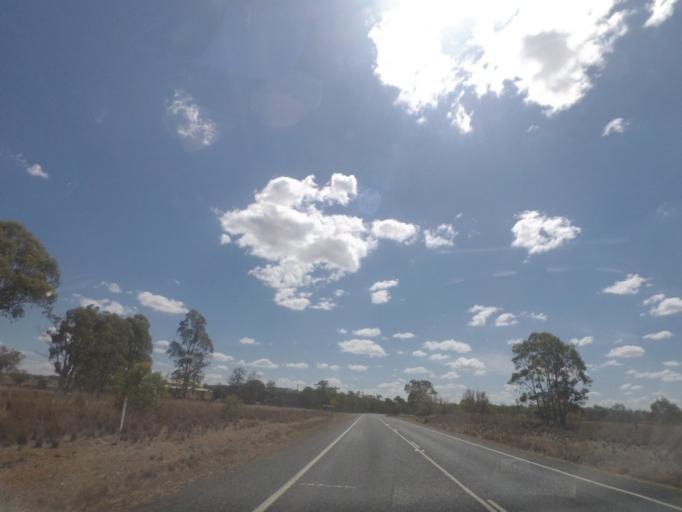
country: AU
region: Queensland
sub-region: Southern Downs
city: Warwick
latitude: -28.1624
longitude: 151.7025
